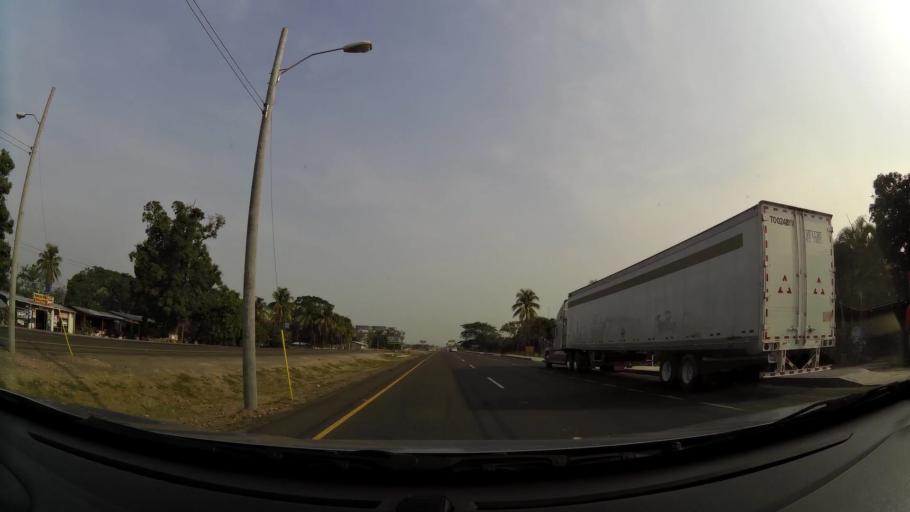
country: HN
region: Comayagua
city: Villa de San Antonio
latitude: 14.3211
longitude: -87.5840
